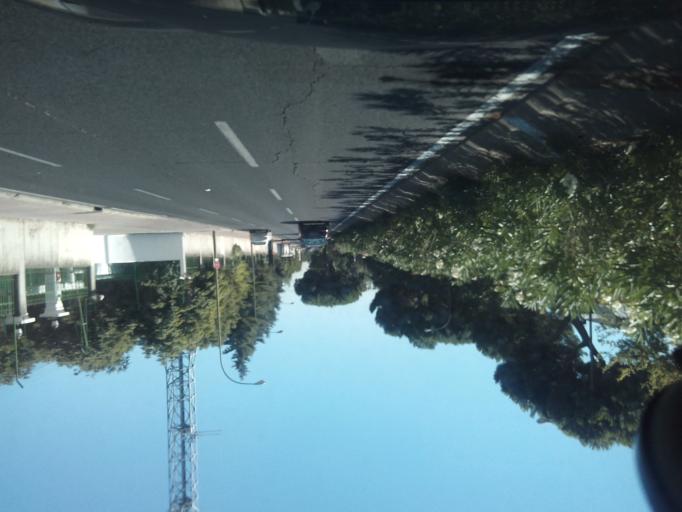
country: ES
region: Madrid
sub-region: Provincia de Madrid
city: Pinar de Chamartin
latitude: 40.4749
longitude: -3.6683
